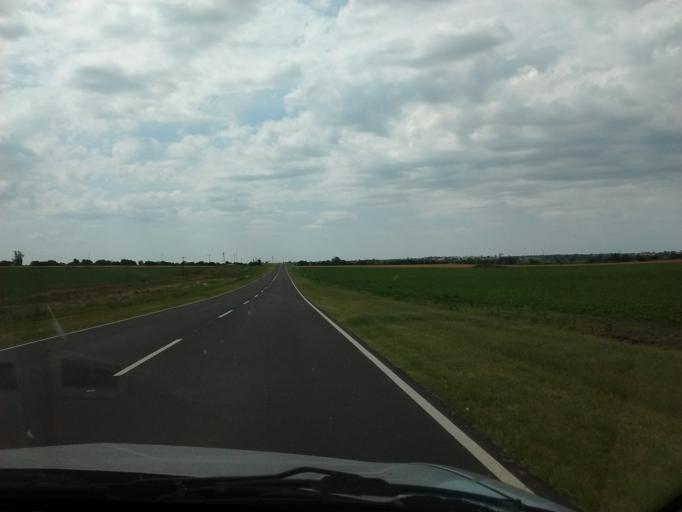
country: AR
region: Entre Rios
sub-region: Departamento de Victoria
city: Victoria
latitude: -32.7973
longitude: -59.8953
